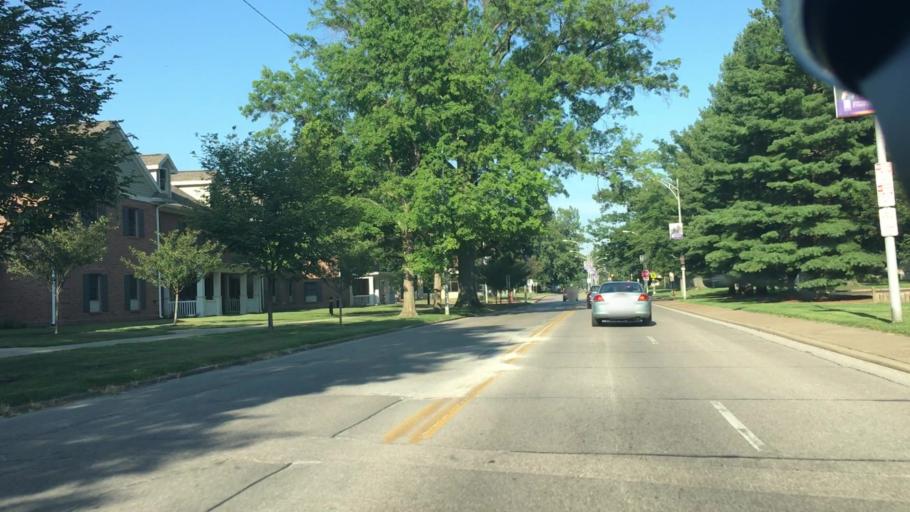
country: US
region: Indiana
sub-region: Vanderburgh County
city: Evansville
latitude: 37.9735
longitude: -87.5351
